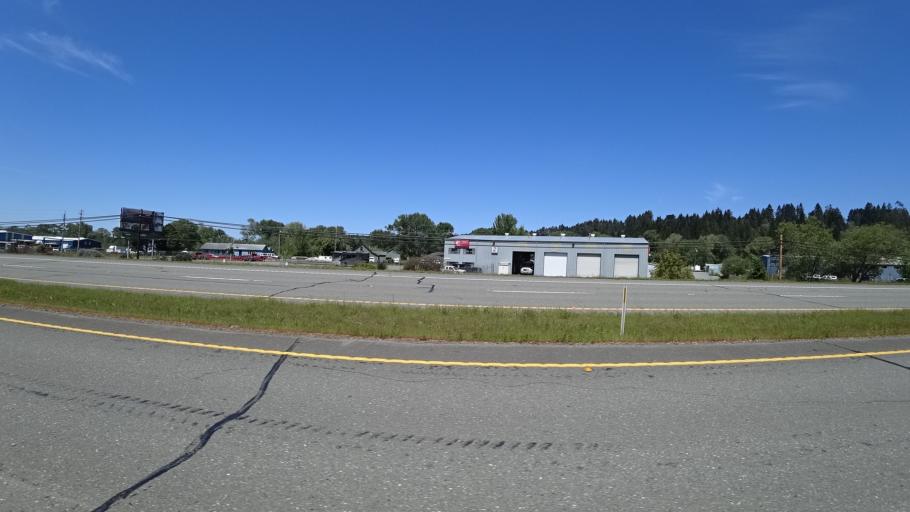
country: US
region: California
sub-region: Humboldt County
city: Arcata
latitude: 40.9096
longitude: -124.0704
